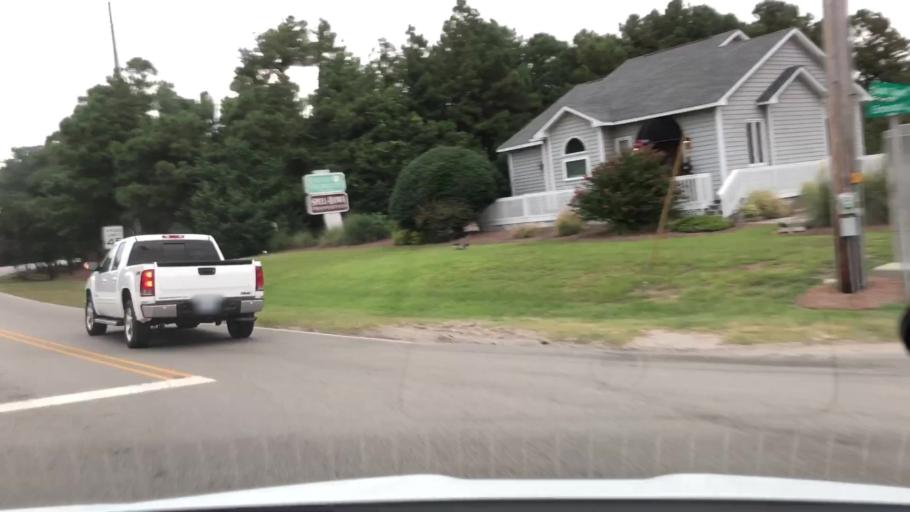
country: US
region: North Carolina
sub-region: Carteret County
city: Cedar Point
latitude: 34.6610
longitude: -77.0598
